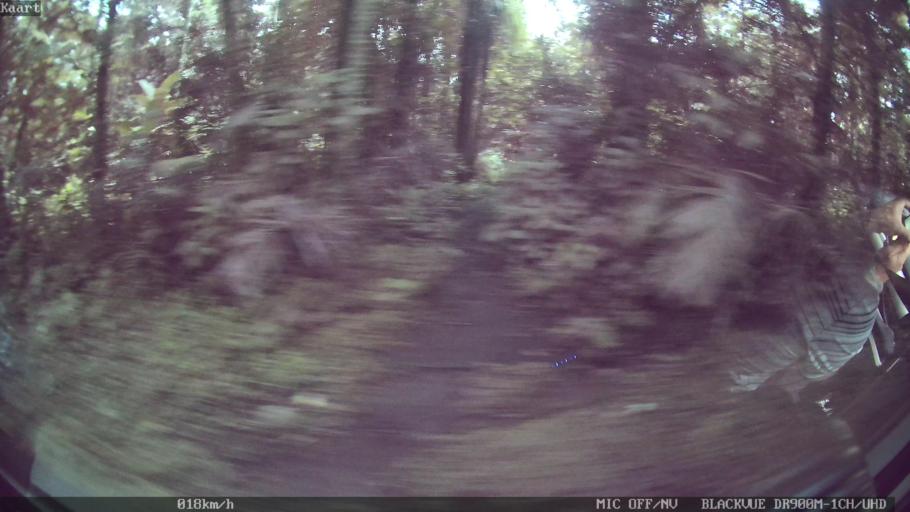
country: ID
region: Bali
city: Bunutan
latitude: -8.4692
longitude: 115.2347
